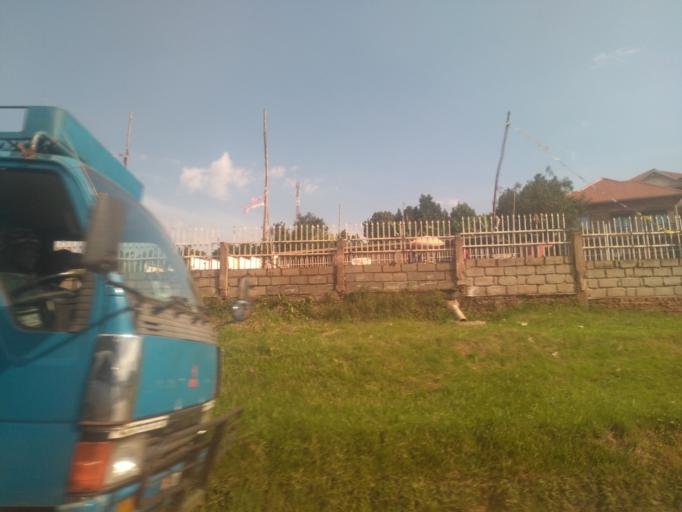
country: UG
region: Central Region
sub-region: Wakiso District
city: Kajansi
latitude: 0.2781
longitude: 32.4693
